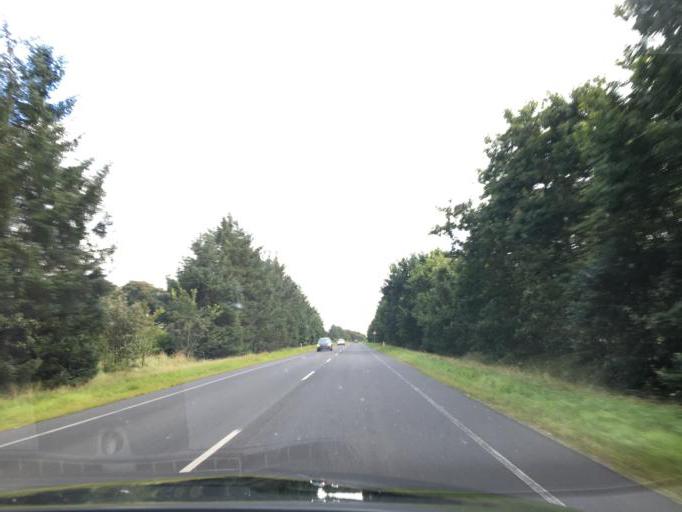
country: DK
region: South Denmark
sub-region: Varde Kommune
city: Olgod
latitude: 55.7994
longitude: 8.6288
